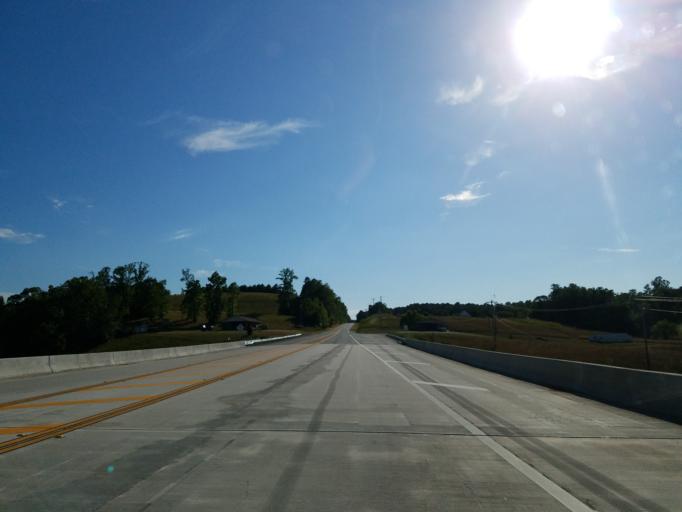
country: US
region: Georgia
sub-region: Gordon County
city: Calhoun
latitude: 34.5762
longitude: -84.9548
